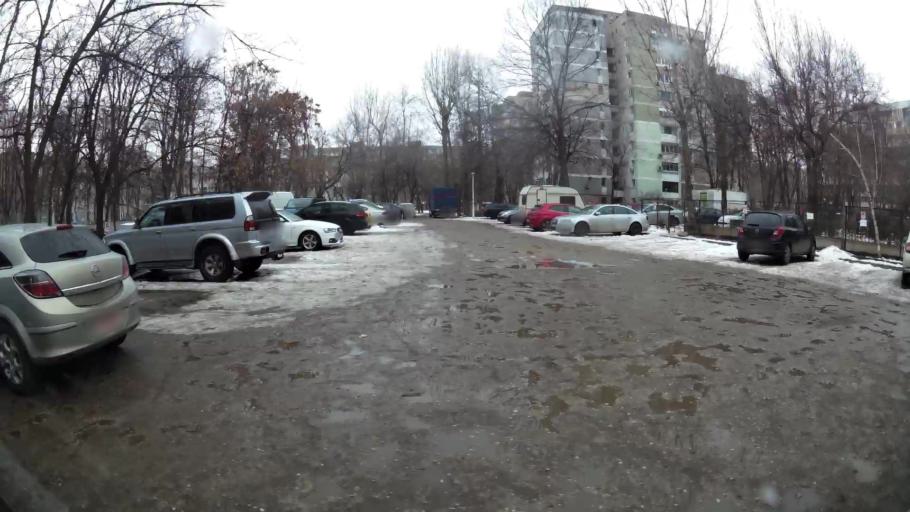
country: RO
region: Ilfov
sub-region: Comuna Chiajna
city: Rosu
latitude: 44.4250
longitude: 26.0299
